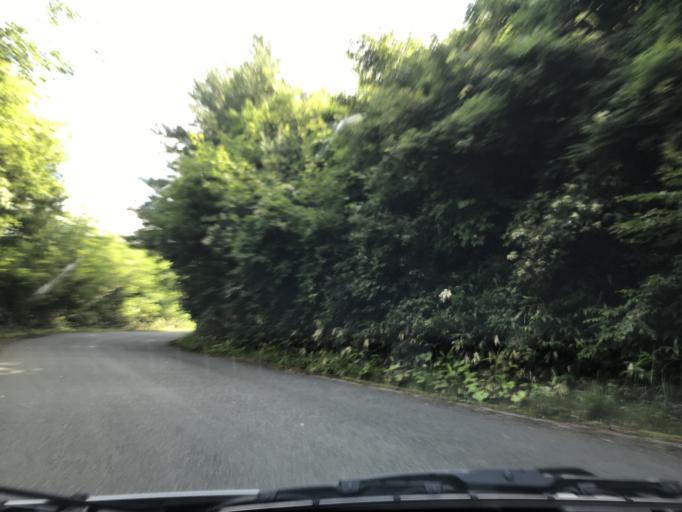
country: JP
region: Iwate
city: Mizusawa
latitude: 39.0267
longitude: 141.1895
